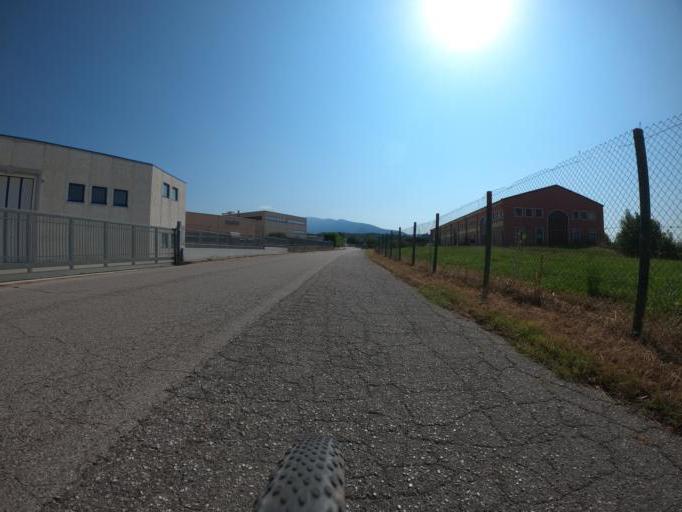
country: IT
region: Veneto
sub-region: Provincia di Verona
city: Costermano
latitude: 45.5839
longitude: 10.7692
